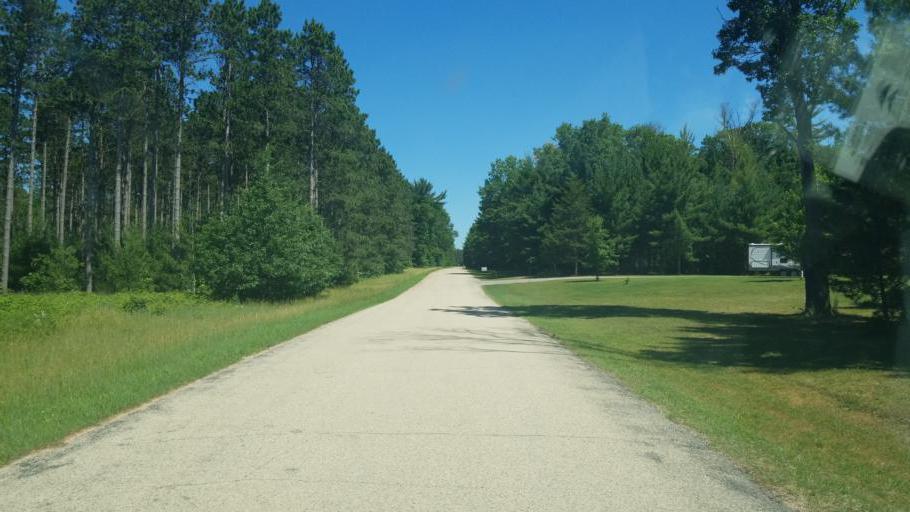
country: US
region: Wisconsin
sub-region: Juneau County
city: Mauston
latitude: 43.8714
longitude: -89.9484
